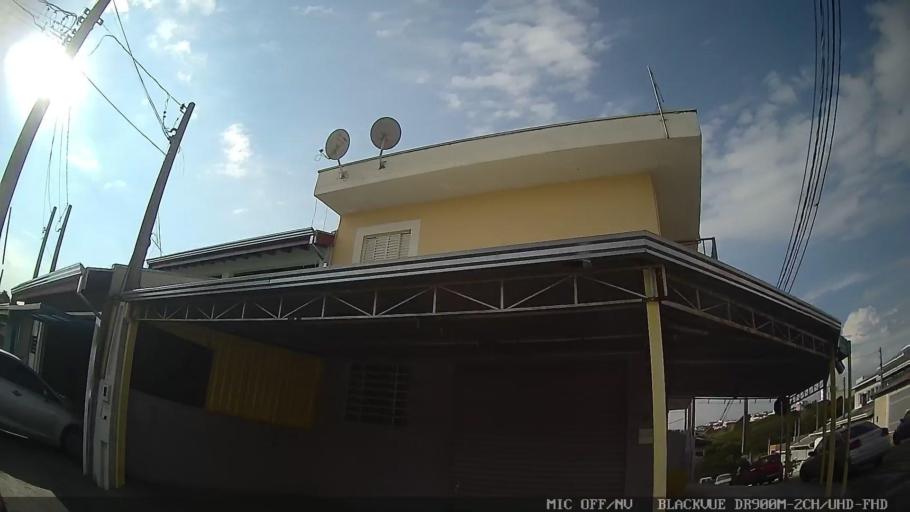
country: BR
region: Sao Paulo
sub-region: Indaiatuba
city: Indaiatuba
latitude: -23.0989
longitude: -47.2417
